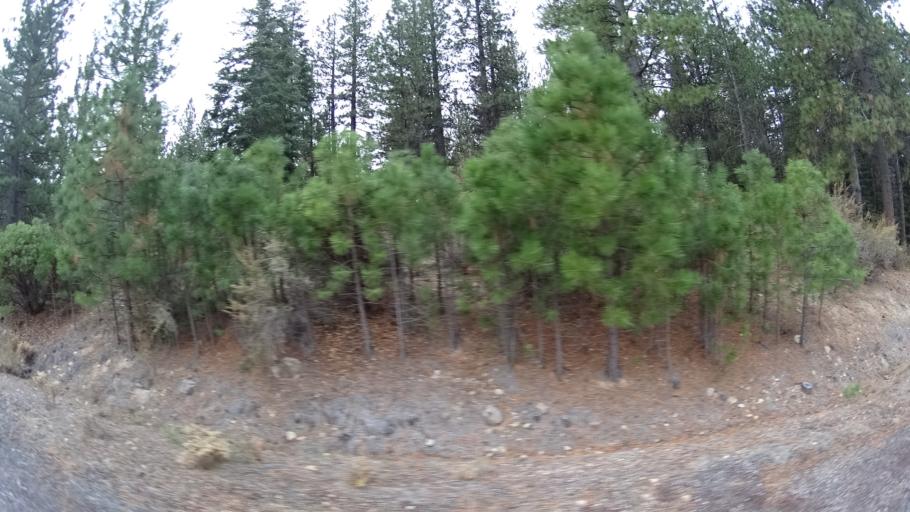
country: US
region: California
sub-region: Siskiyou County
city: Weed
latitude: 41.4089
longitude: -122.3738
